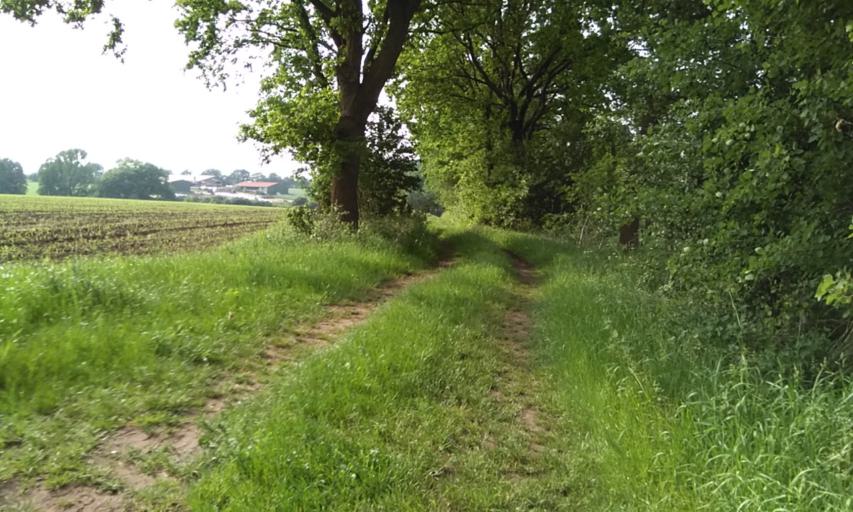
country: DE
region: Lower Saxony
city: Nottensdorf
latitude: 53.4663
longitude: 9.6238
